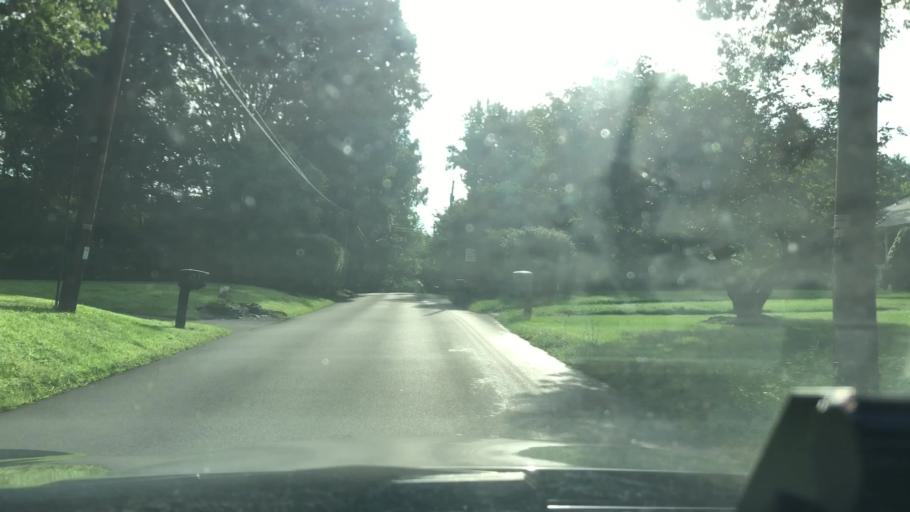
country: US
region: Pennsylvania
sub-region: Northampton County
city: Bethlehem
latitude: 40.6557
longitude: -75.3656
